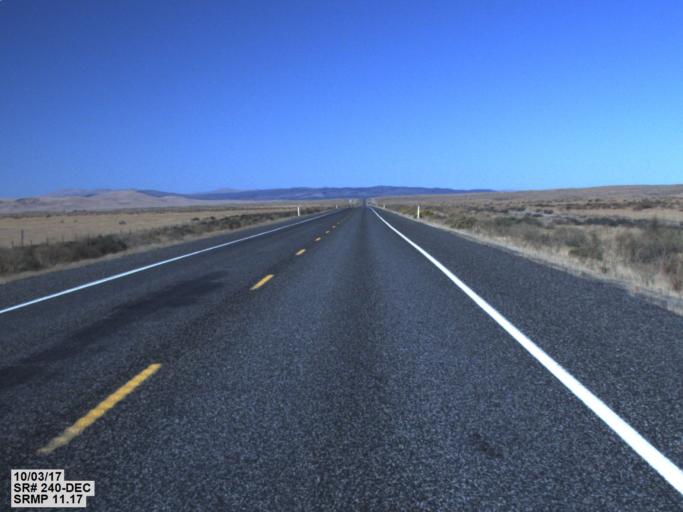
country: US
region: Washington
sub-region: Benton County
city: Benton City
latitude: 46.4761
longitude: -119.5607
